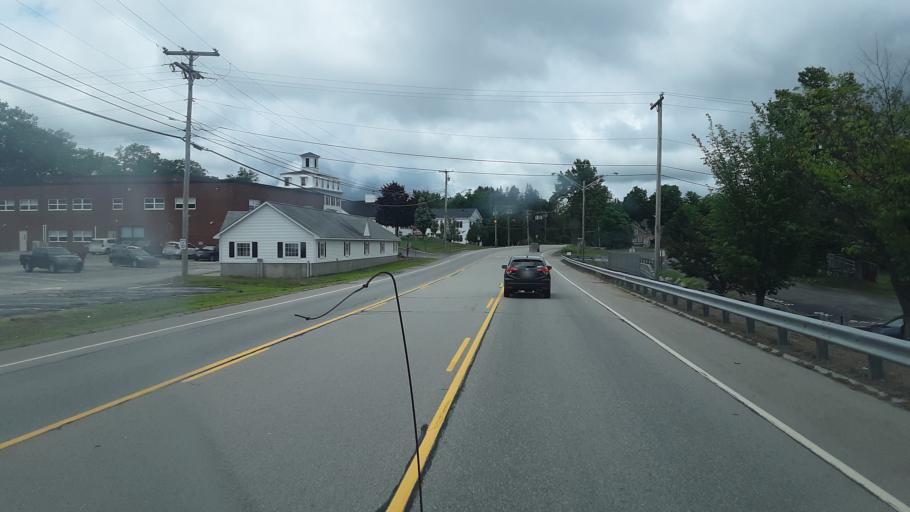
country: US
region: New Hampshire
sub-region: Rockingham County
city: Northwood
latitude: 43.2179
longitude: -71.2096
